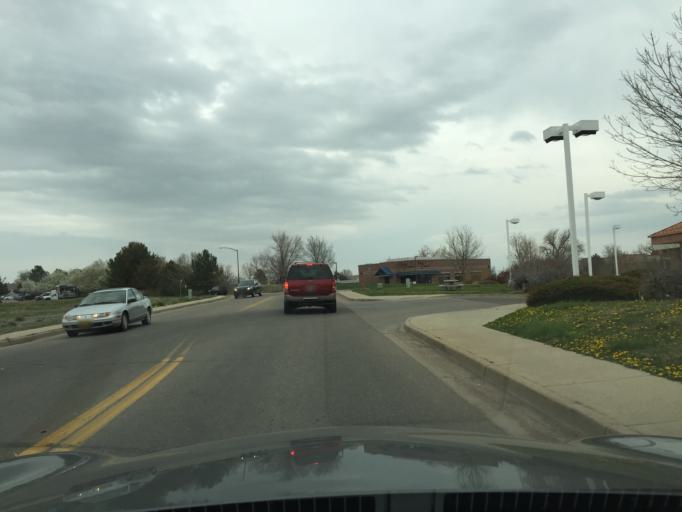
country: US
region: Colorado
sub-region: Boulder County
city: Lafayette
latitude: 40.0005
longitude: -105.1051
